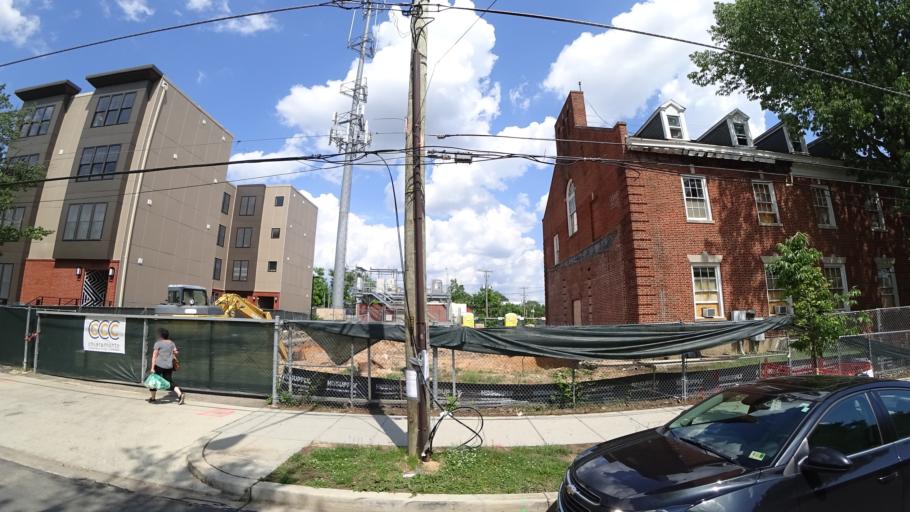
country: US
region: Maryland
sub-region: Prince George's County
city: Mount Rainier
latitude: 38.9274
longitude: -76.9807
